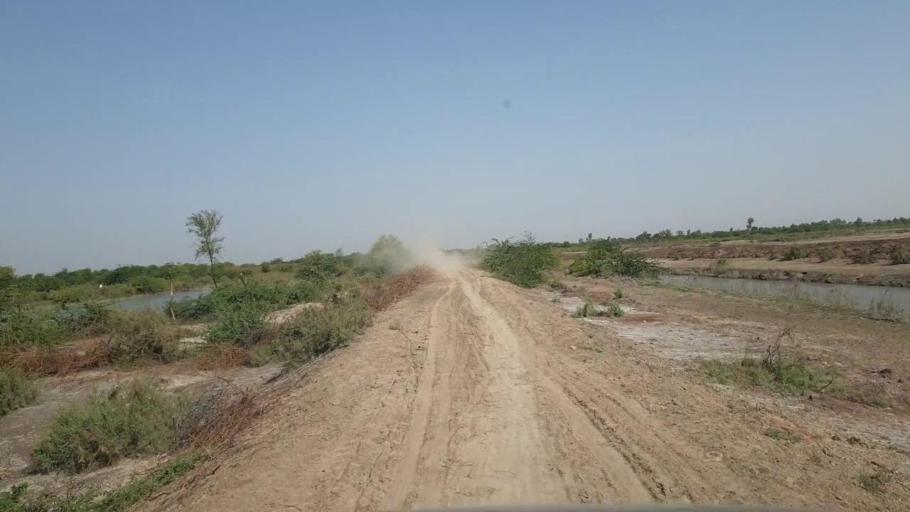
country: PK
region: Sindh
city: Tando Bago
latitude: 24.6705
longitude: 69.0683
